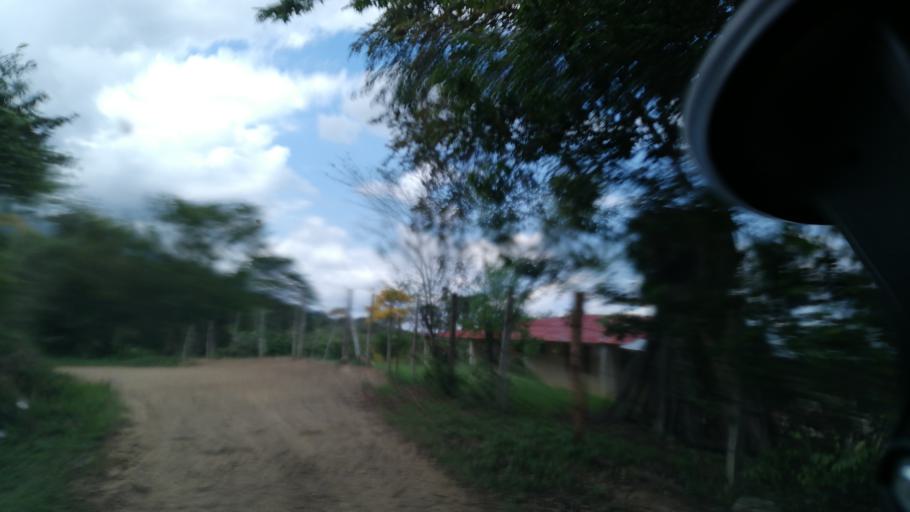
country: CO
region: Cundinamarca
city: Viani
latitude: 4.8146
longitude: -74.6164
